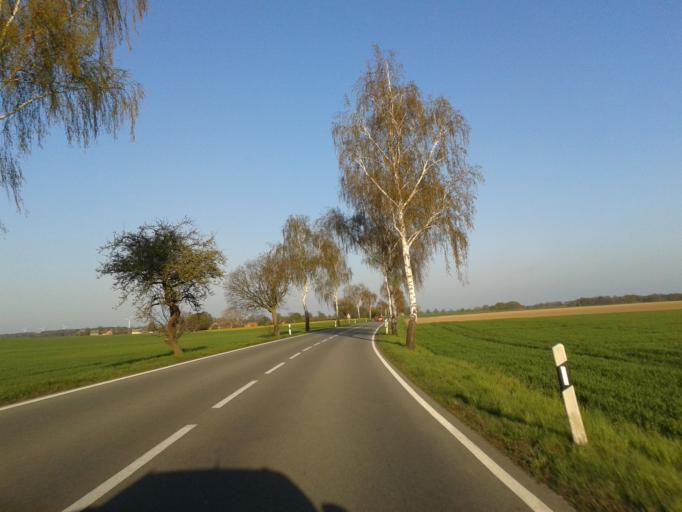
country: DE
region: Lower Saxony
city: Kusten
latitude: 52.9446
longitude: 11.0522
